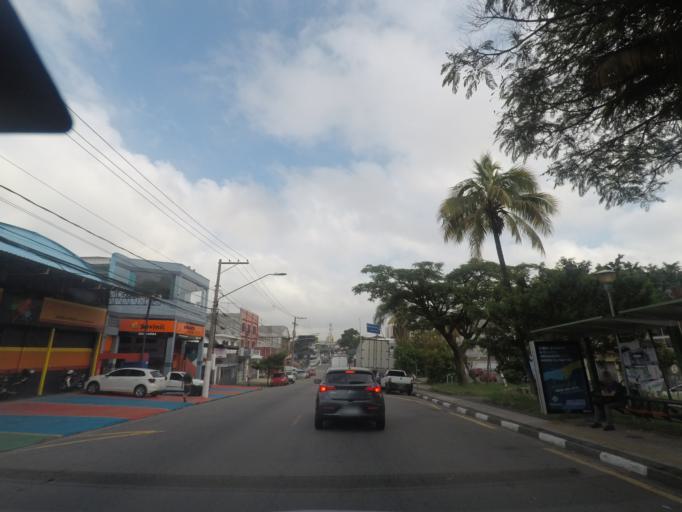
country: BR
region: Sao Paulo
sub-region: Osasco
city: Osasco
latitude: -23.5665
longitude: -46.7805
